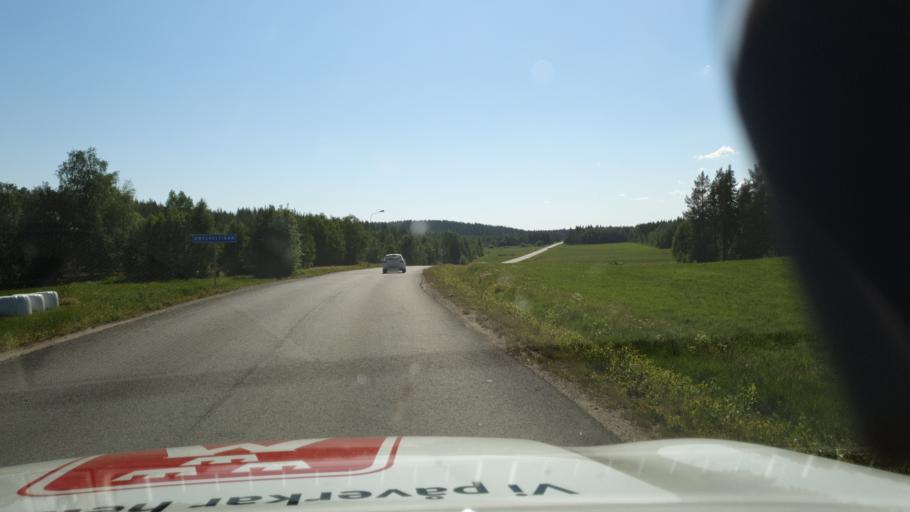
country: SE
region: Vaesterbotten
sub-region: Vindelns Kommun
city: Vindeln
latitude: 64.2431
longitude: 19.8298
